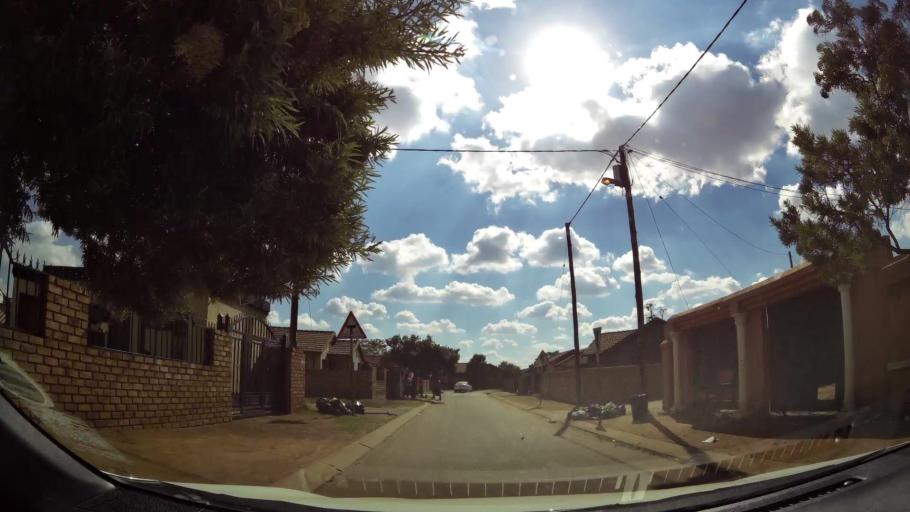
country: ZA
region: Gauteng
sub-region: City of Tshwane Metropolitan Municipality
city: Cullinan
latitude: -25.7038
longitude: 28.4094
